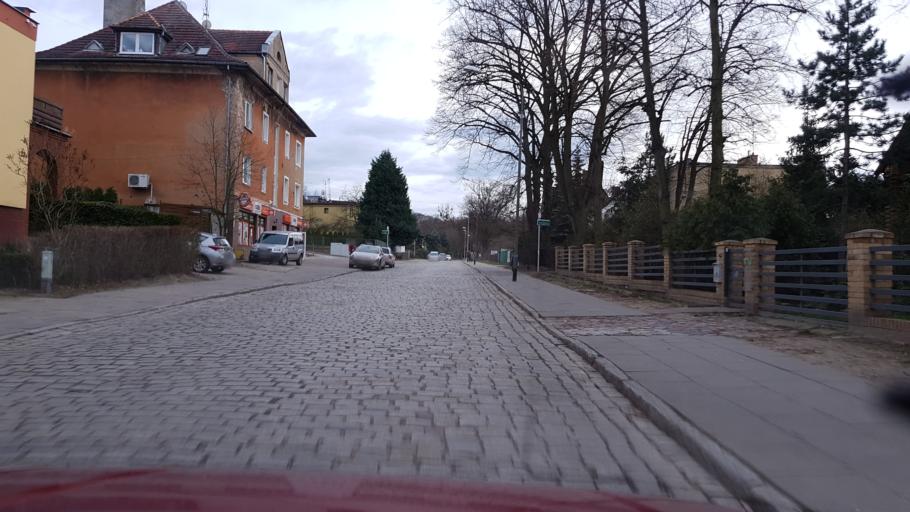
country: PL
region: West Pomeranian Voivodeship
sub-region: Szczecin
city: Szczecin
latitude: 53.3634
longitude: 14.5976
